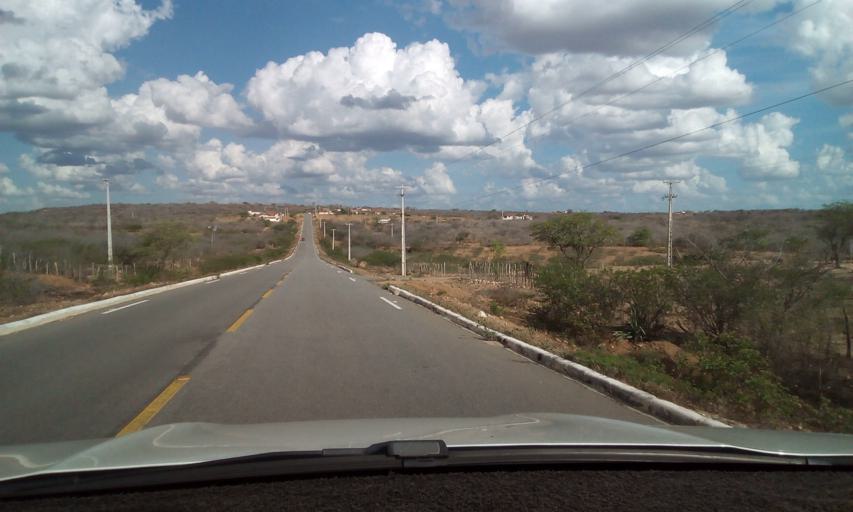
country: BR
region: Rio Grande do Norte
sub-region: Parelhas
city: Parelhas
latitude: -6.7951
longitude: -36.4139
